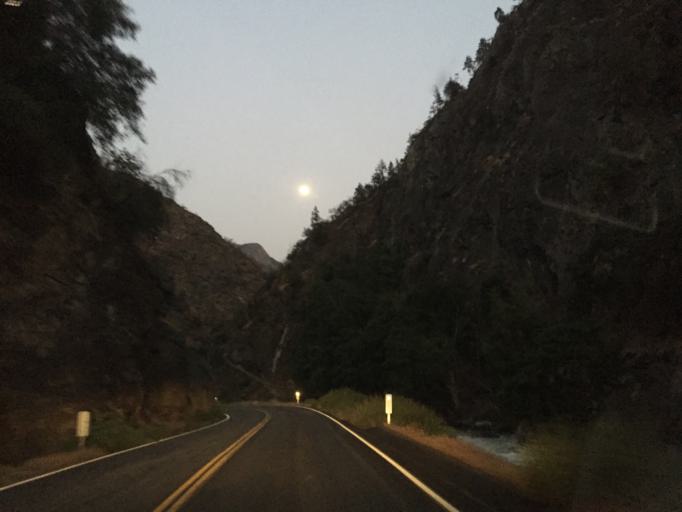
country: US
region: California
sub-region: Tulare County
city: Three Rivers
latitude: 36.8163
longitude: -118.8189
